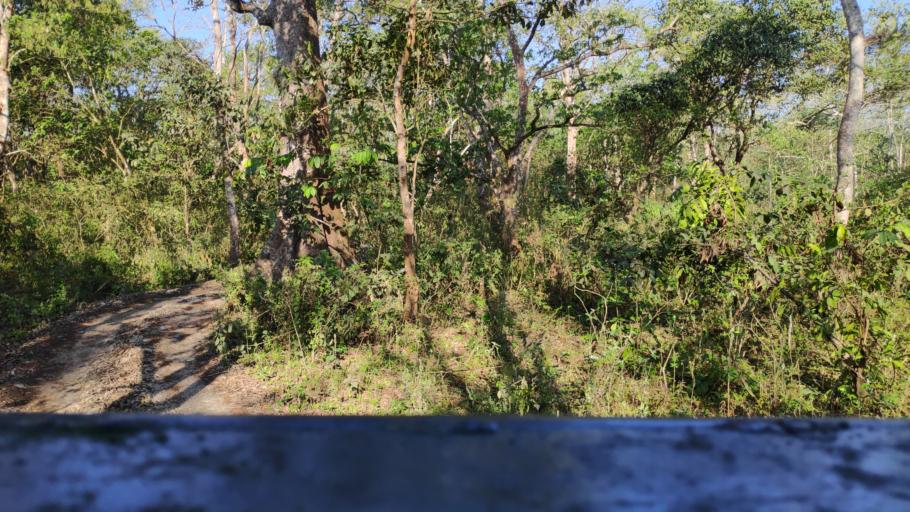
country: NP
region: Central Region
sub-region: Narayani Zone
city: Bharatpur
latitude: 27.5583
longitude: 84.5488
